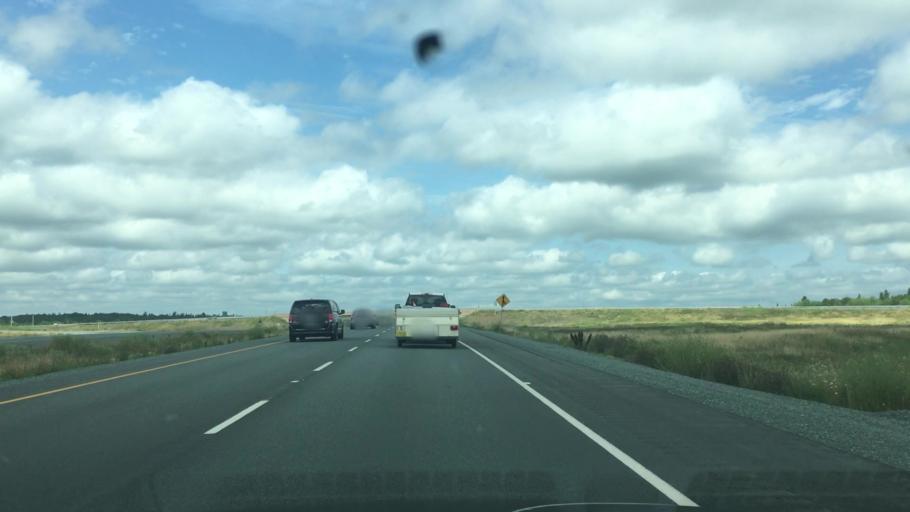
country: CA
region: Nova Scotia
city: Oxford
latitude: 45.6921
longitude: -63.7724
